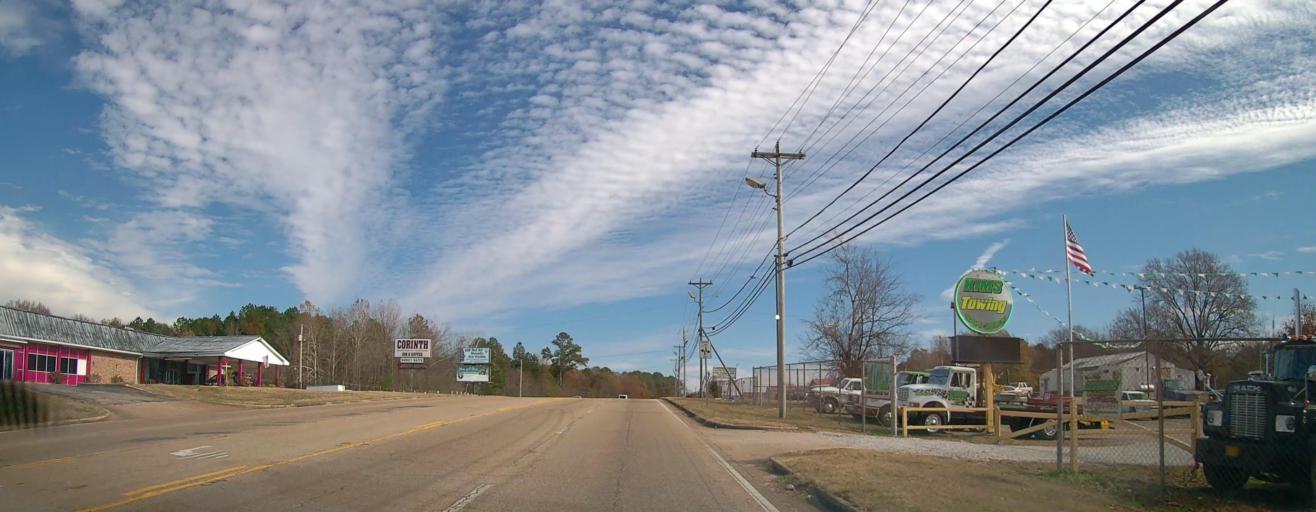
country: US
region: Mississippi
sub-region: Alcorn County
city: Corinth
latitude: 34.9307
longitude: -88.5410
